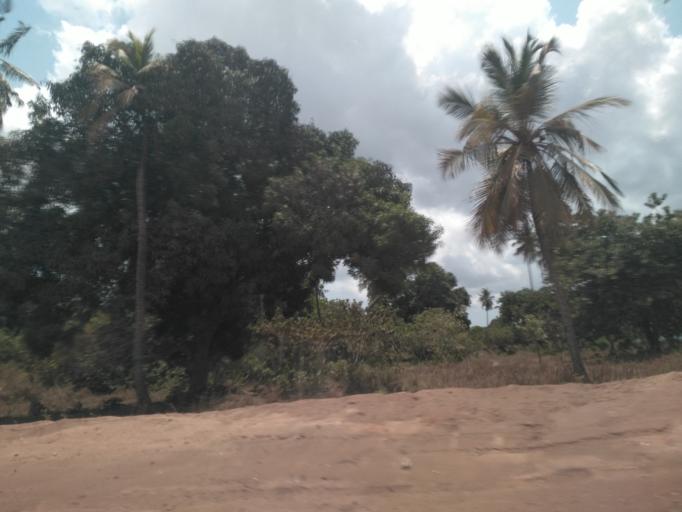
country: TZ
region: Dar es Salaam
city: Dar es Salaam
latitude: -6.8669
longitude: 39.3291
